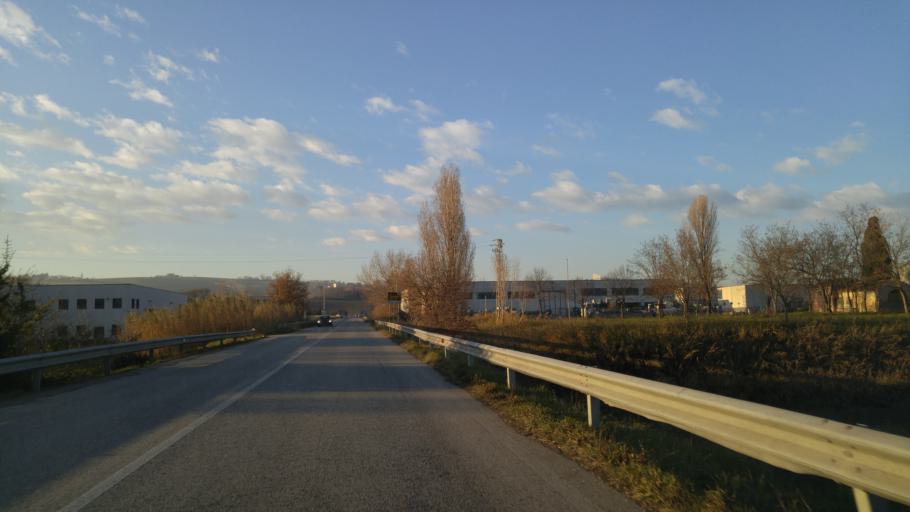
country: IT
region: The Marches
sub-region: Provincia di Ancona
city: Monterado
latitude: 43.7079
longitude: 13.0784
